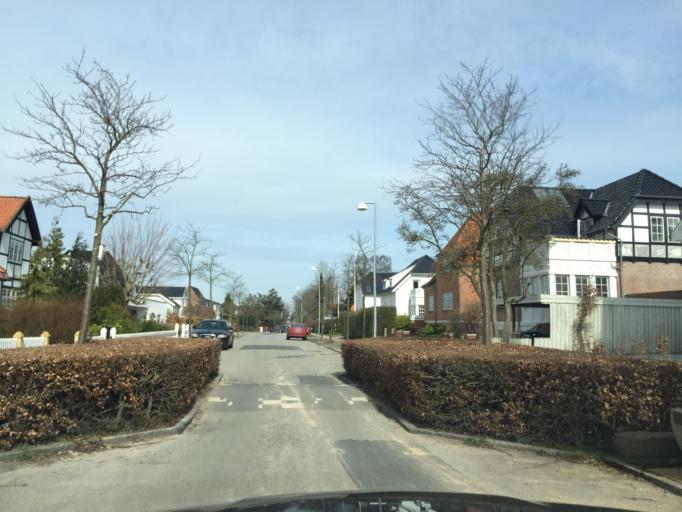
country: DK
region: South Denmark
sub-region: Odense Kommune
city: Odense
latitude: 55.3774
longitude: 10.3765
